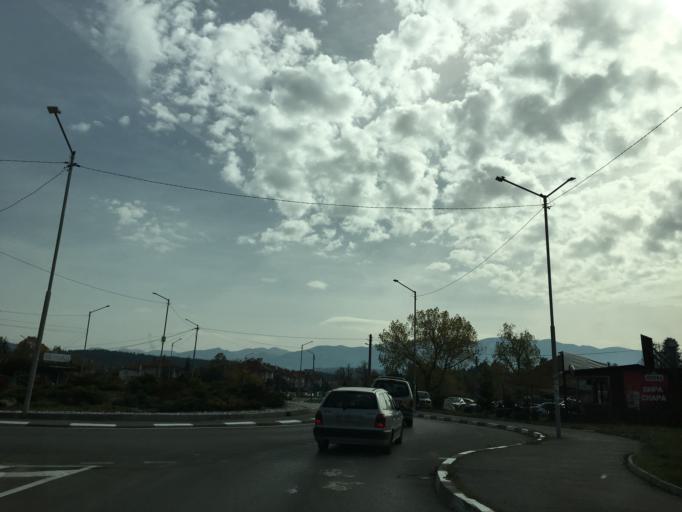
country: BG
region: Sofiya
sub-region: Obshtina Samokov
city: Samokov
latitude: 42.3264
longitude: 23.5593
